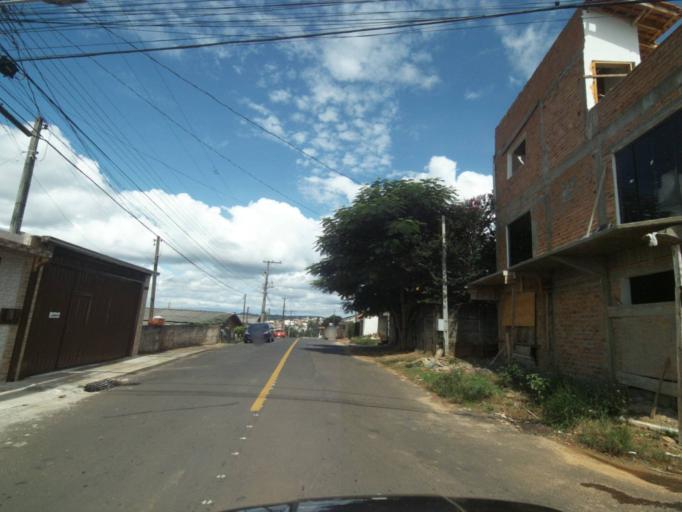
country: BR
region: Parana
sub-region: Telemaco Borba
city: Telemaco Borba
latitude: -24.3152
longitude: -50.6276
